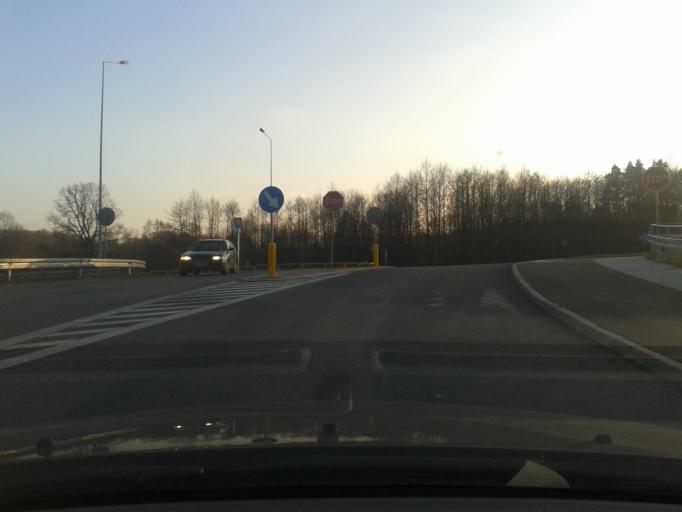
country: PL
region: Lublin Voivodeship
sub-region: Powiat opolski
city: Opole Lubelskie
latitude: 51.1315
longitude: 22.0119
